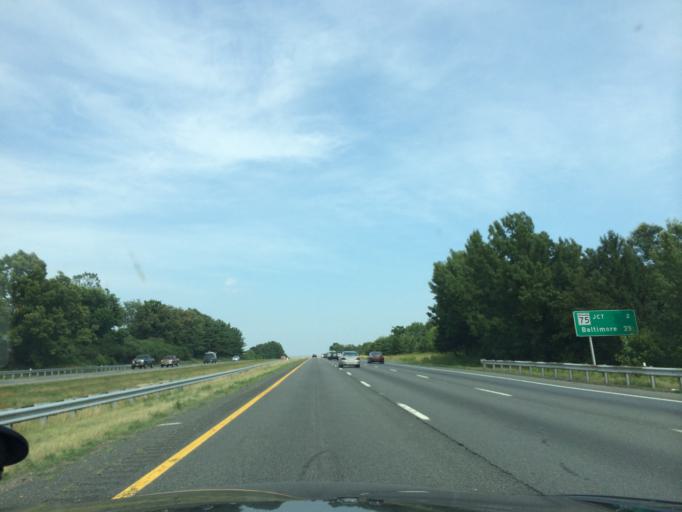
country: US
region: Maryland
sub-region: Frederick County
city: Spring Ridge
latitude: 39.3874
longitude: -77.3063
